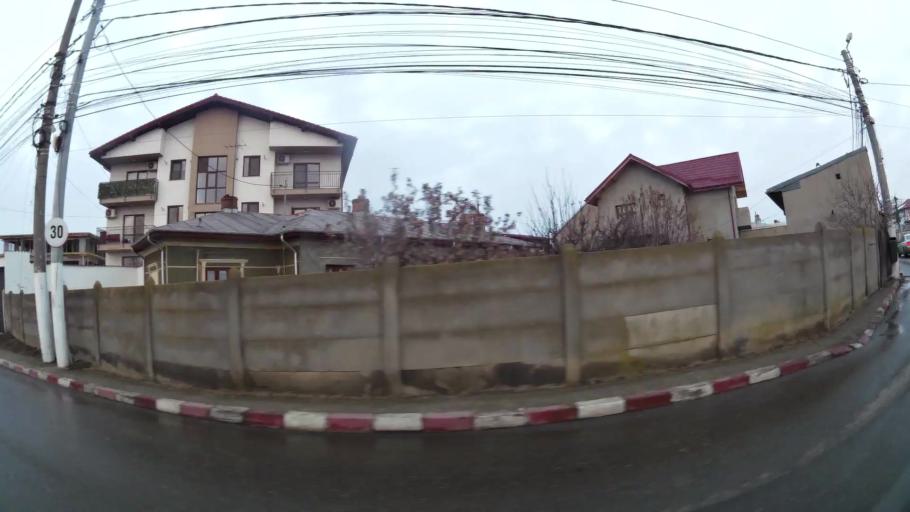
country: RO
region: Ilfov
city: Dobroesti
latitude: 44.4547
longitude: 26.1787
